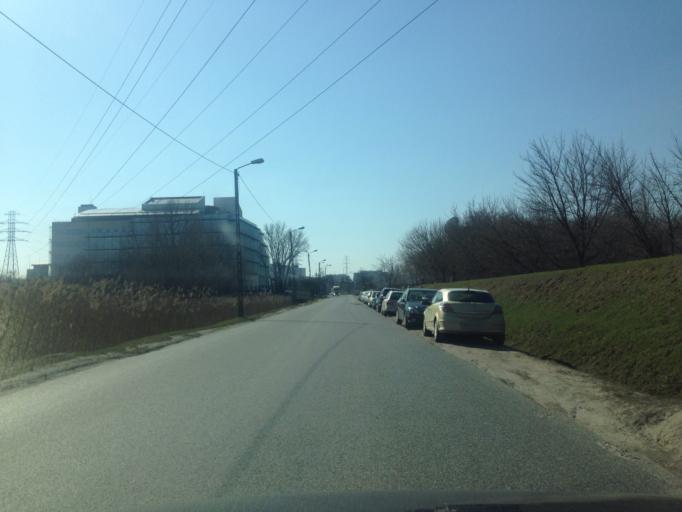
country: PL
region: Masovian Voivodeship
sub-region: Warszawa
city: Wilanow
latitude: 52.1813
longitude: 21.0753
